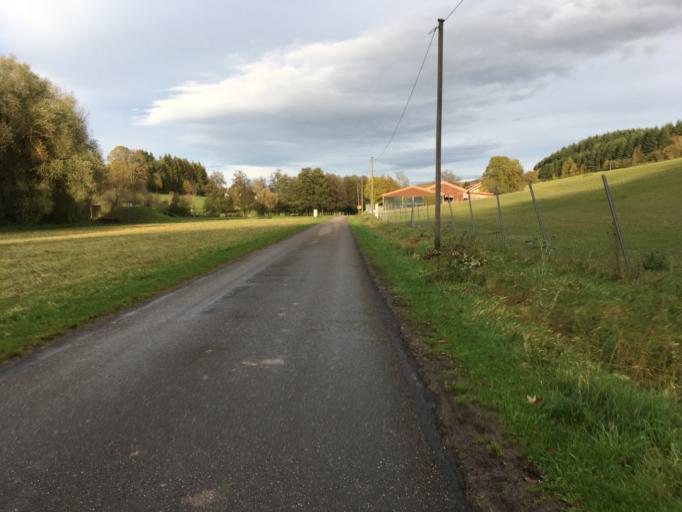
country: DE
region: Baden-Wuerttemberg
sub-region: Regierungsbezirk Stuttgart
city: Jagsthausen
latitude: 49.3587
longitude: 9.4753
